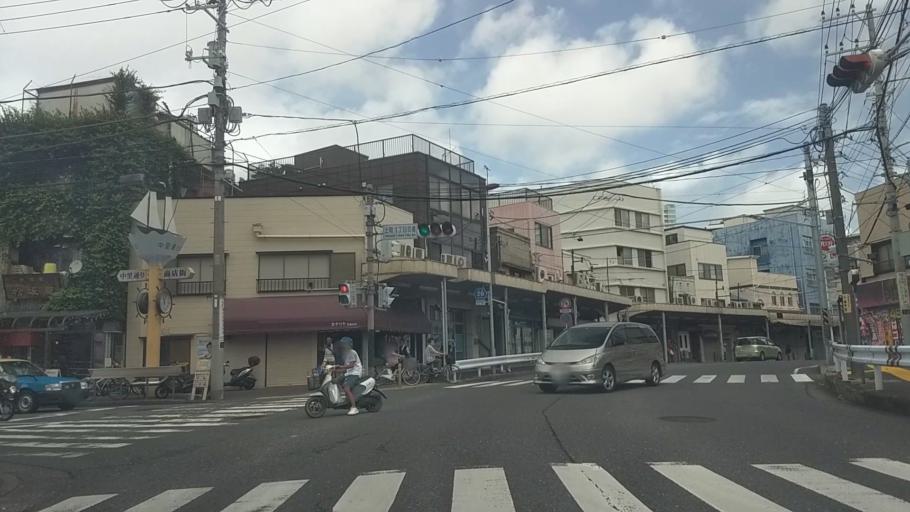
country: JP
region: Kanagawa
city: Yokosuka
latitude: 35.2756
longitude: 139.6697
